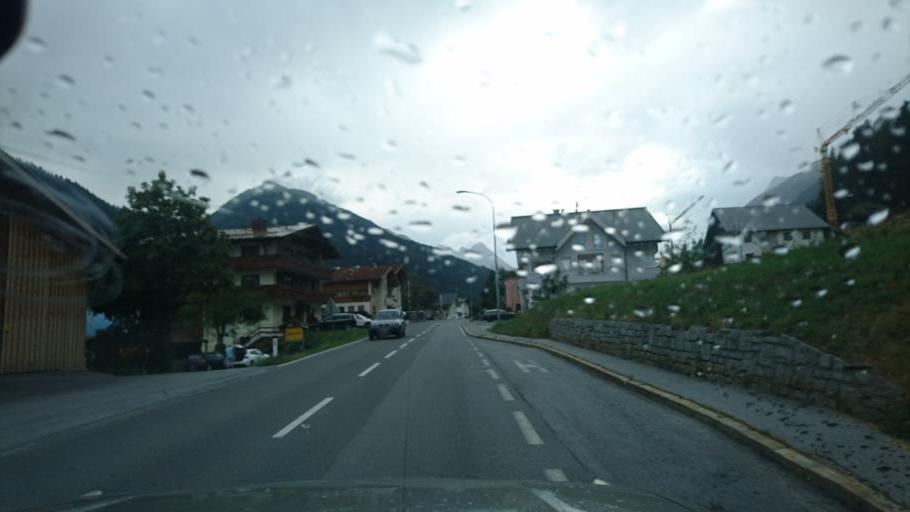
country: AT
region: Tyrol
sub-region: Politischer Bezirk Landeck
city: Ischgl
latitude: 46.9900
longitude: 10.2484
